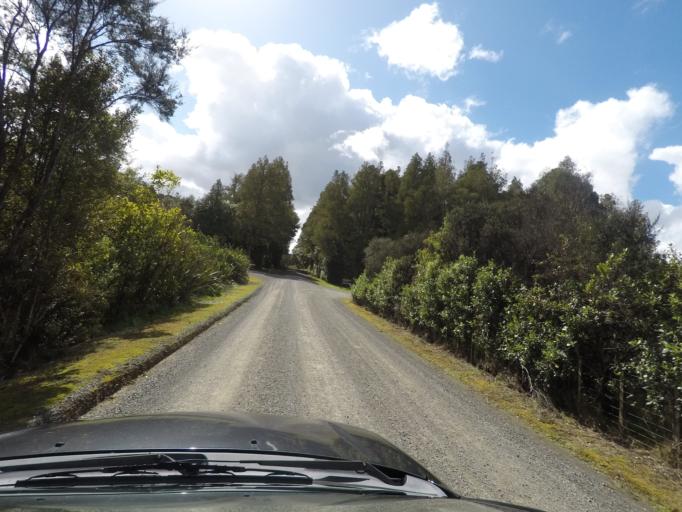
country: NZ
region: Auckland
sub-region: Auckland
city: Red Hill
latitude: -37.0914
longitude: 175.1535
